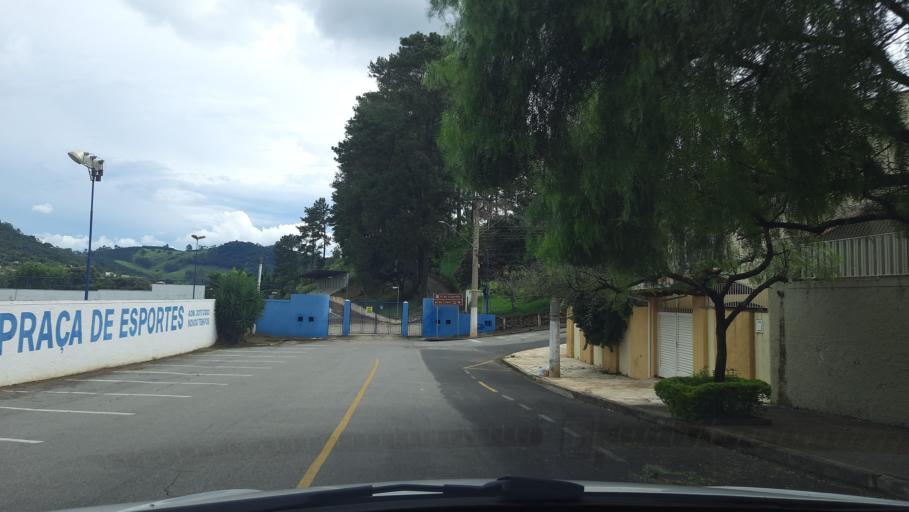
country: BR
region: Sao Paulo
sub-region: Sao Joao Da Boa Vista
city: Sao Joao da Boa Vista
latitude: -21.9411
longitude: -46.7200
